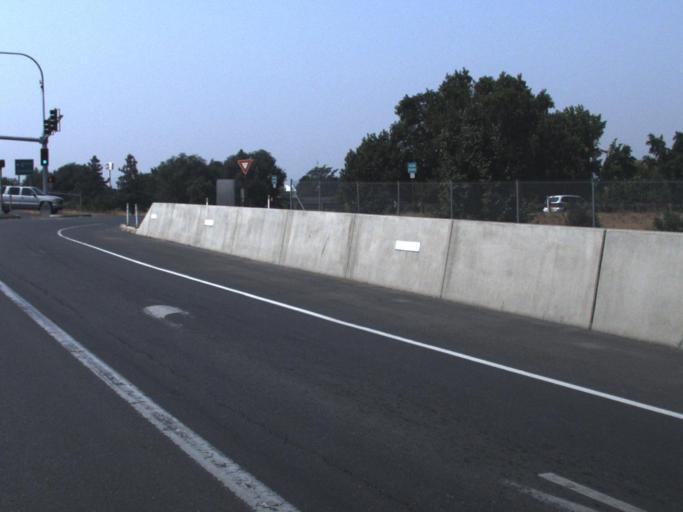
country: US
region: Washington
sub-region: Yakima County
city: Union Gap
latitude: 46.5850
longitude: -120.4710
